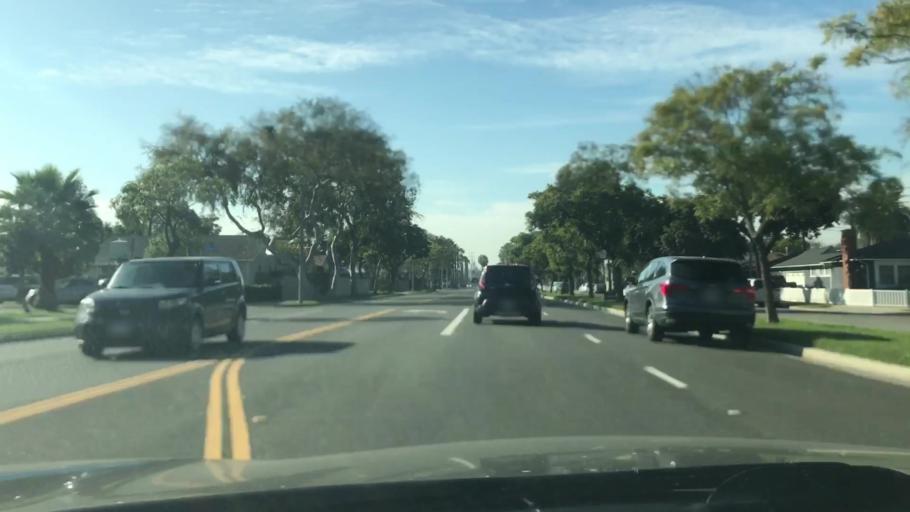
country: US
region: California
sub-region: Orange County
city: Rossmoor
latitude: 33.7960
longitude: -118.1193
